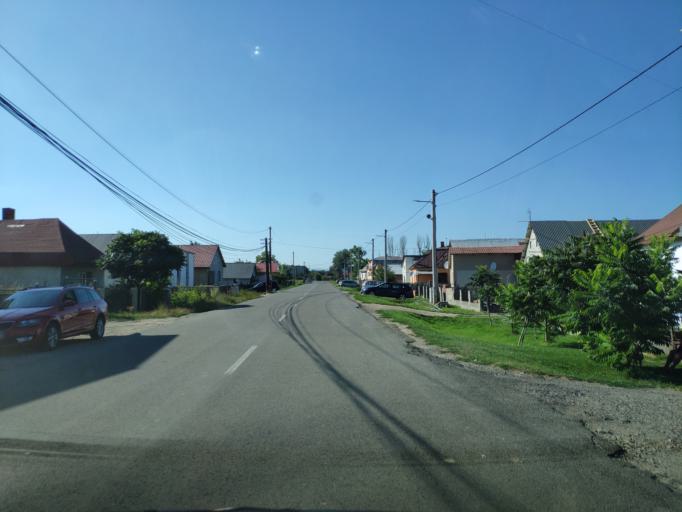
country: SK
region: Kosicky
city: Trebisov
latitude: 48.5709
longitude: 21.8583
